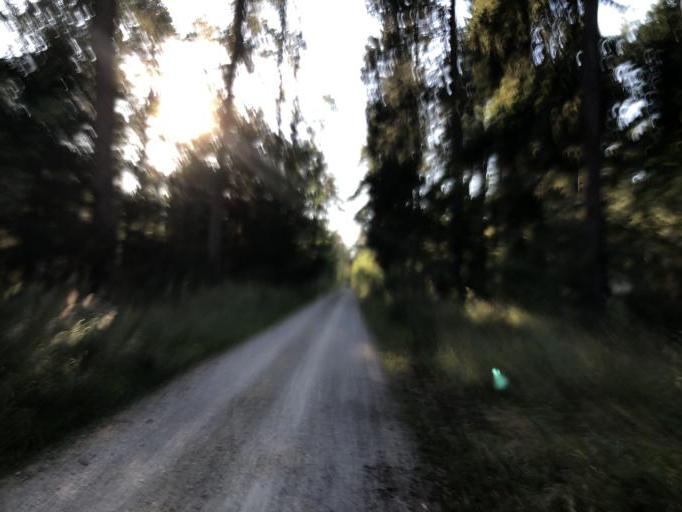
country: DE
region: Bavaria
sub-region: Regierungsbezirk Mittelfranken
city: Kalchreuth
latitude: 49.5577
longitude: 11.1024
